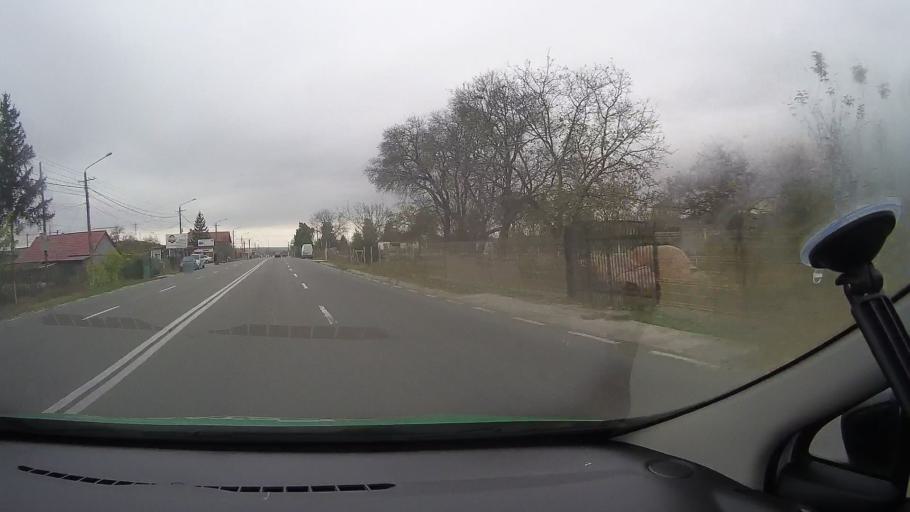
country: RO
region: Constanta
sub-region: Comuna Valu lui Traian
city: Valu lui Traian
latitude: 44.1694
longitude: 28.4408
